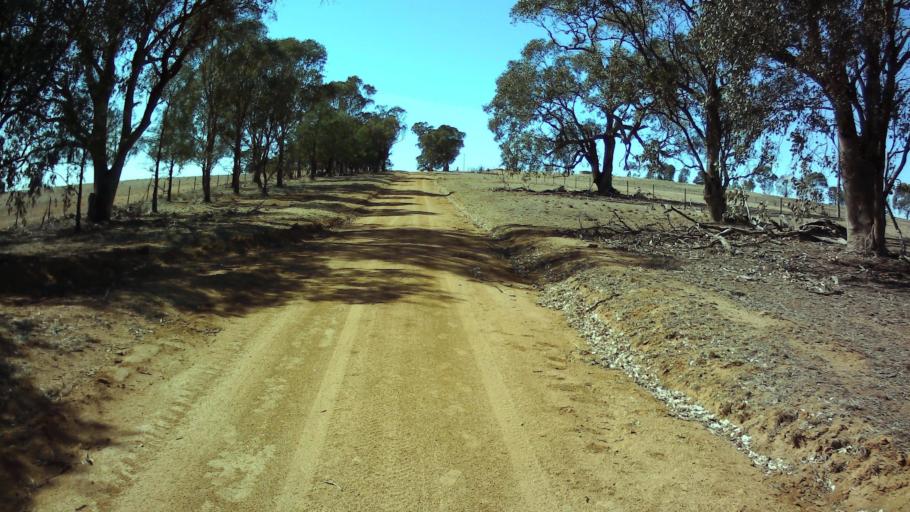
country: AU
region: New South Wales
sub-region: Cowra
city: Cowra
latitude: -33.9729
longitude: 148.4615
